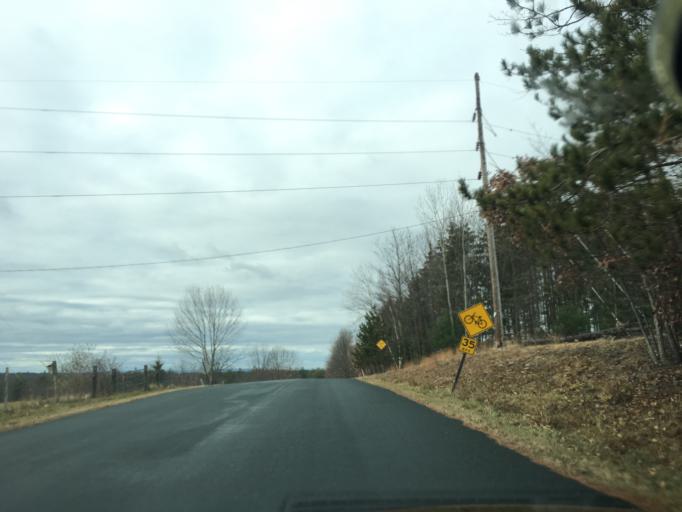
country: US
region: New York
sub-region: Rensselaer County
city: Averill Park
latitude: 42.6106
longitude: -73.5452
